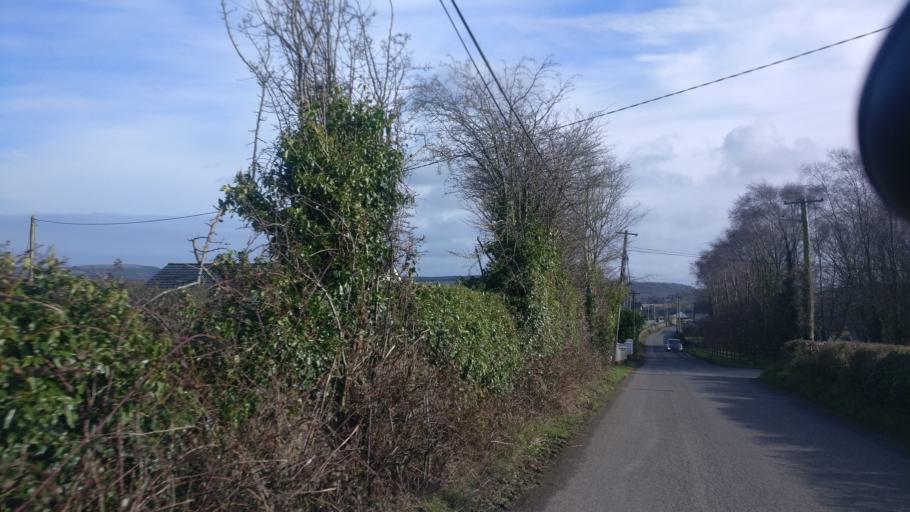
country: IE
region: Leinster
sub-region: Kilkenny
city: Thomastown
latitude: 52.5256
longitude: -7.1616
